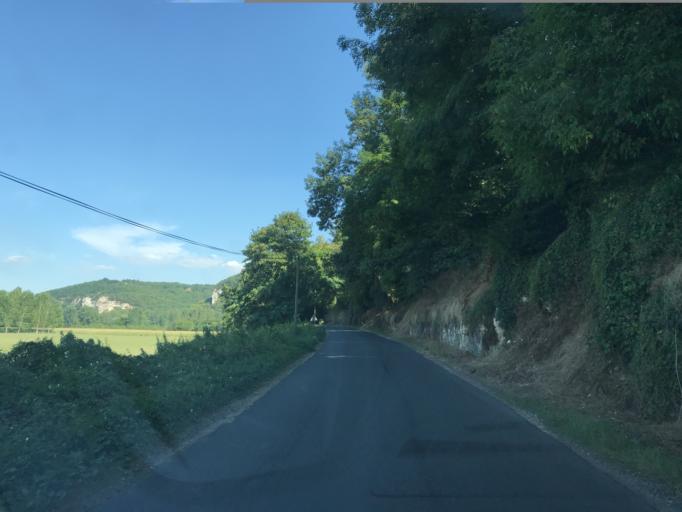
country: FR
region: Aquitaine
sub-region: Departement de la Dordogne
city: Carsac-Aillac
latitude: 44.8233
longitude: 1.2377
